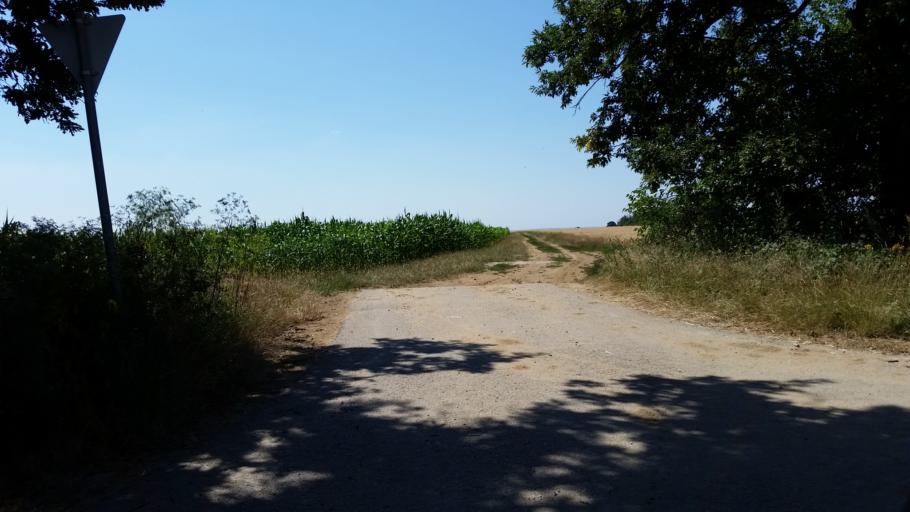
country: HU
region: Fejer
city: Many
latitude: 47.5418
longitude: 18.6078
